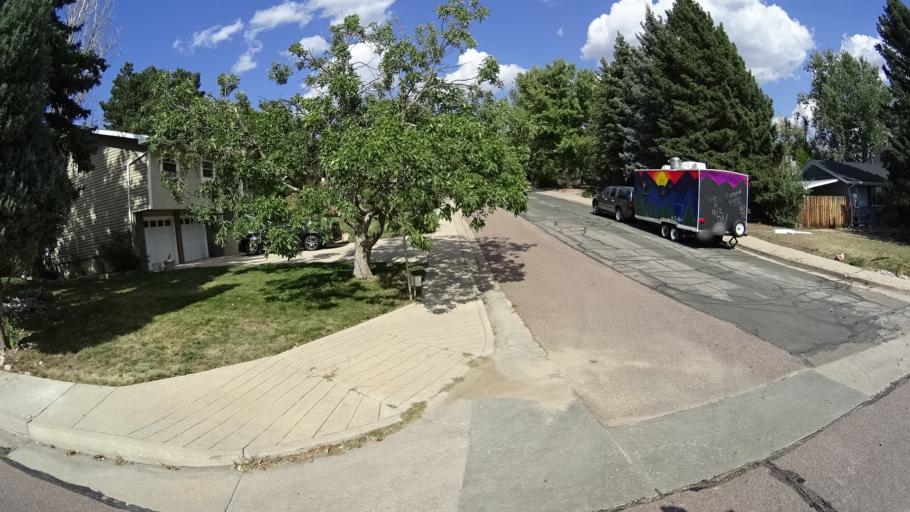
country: US
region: Colorado
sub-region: El Paso County
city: Cimarron Hills
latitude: 38.8716
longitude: -104.7317
